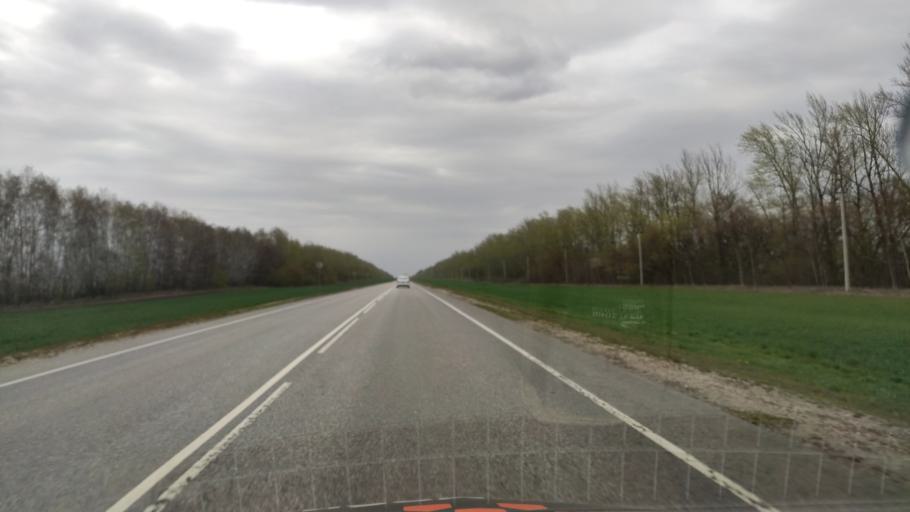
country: RU
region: Kursk
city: Gorshechnoye
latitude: 51.5494
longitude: 38.1565
